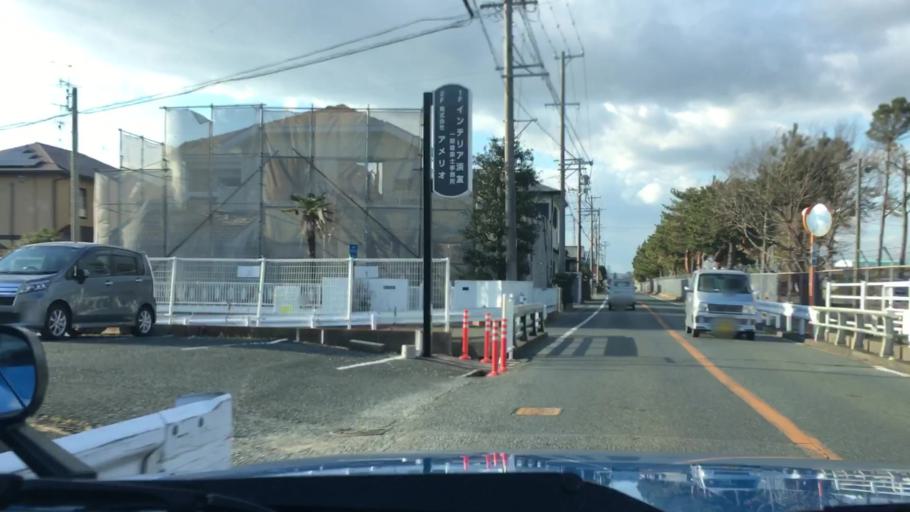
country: JP
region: Shizuoka
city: Hamamatsu
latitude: 34.7438
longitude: 137.6907
